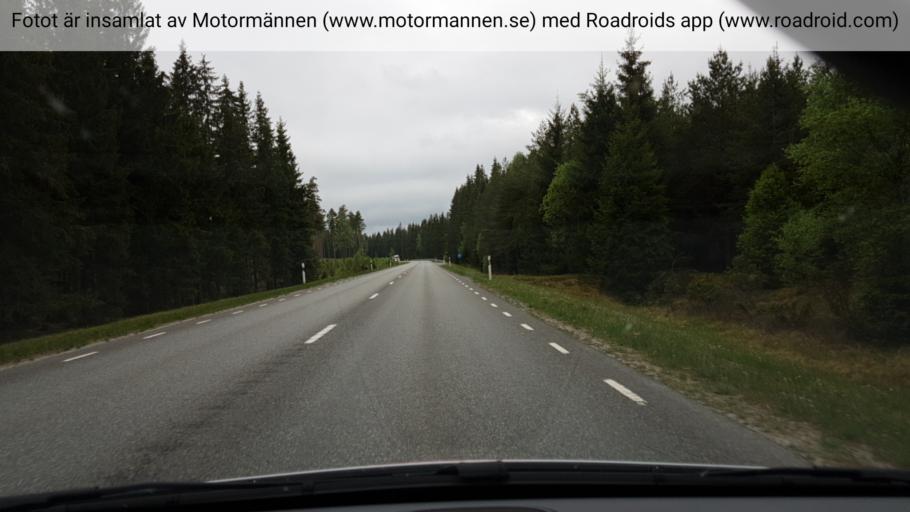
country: SE
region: Joenkoeping
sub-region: Gnosjo Kommun
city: Marieholm
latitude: 57.6319
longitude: 13.7831
